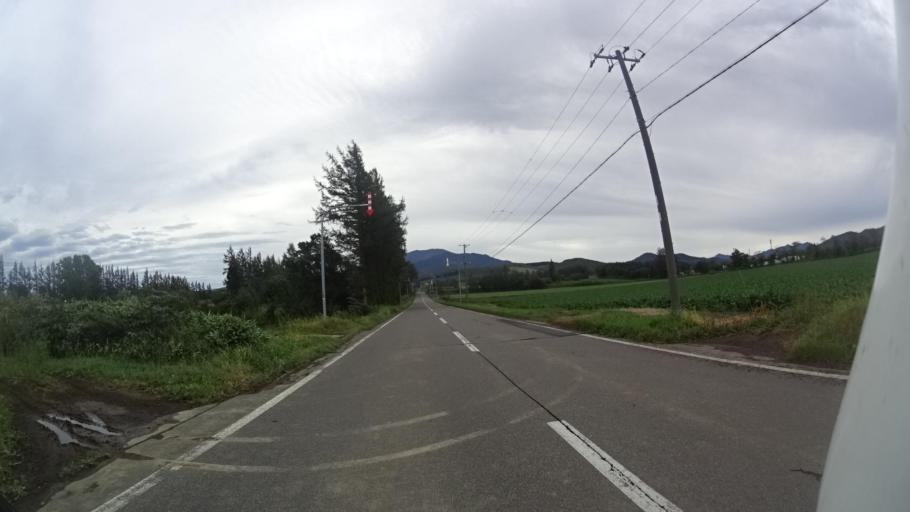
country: JP
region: Hokkaido
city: Shibetsu
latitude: 43.8742
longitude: 144.7423
